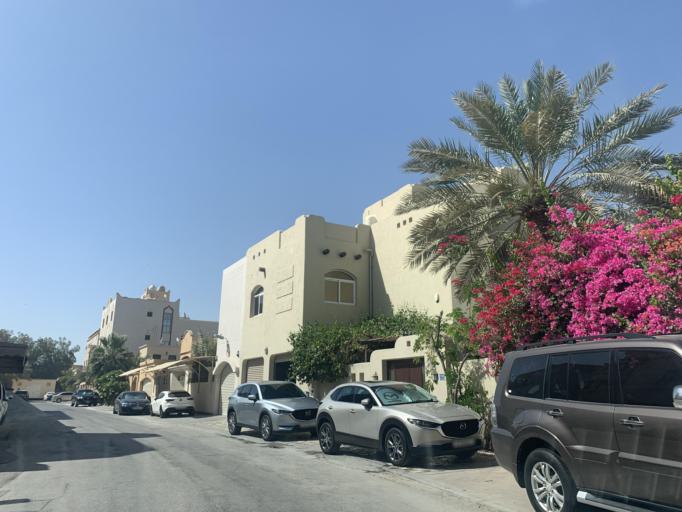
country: BH
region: Manama
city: Jidd Hafs
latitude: 26.2241
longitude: 50.5267
